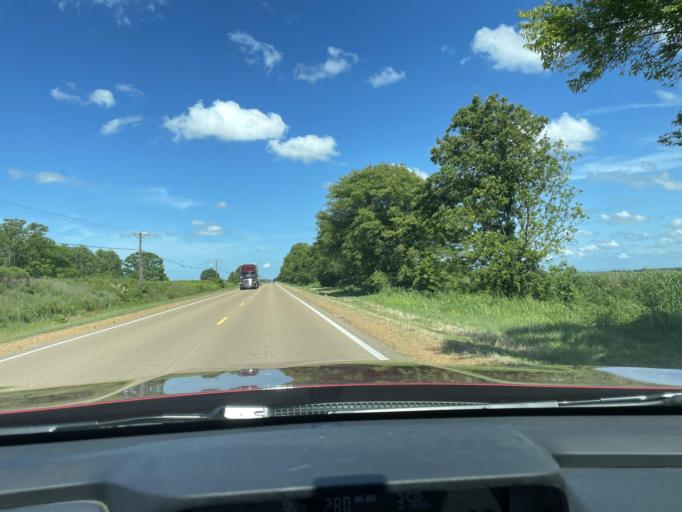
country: US
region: Mississippi
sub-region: Humphreys County
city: Belzoni
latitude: 33.1837
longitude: -90.5840
